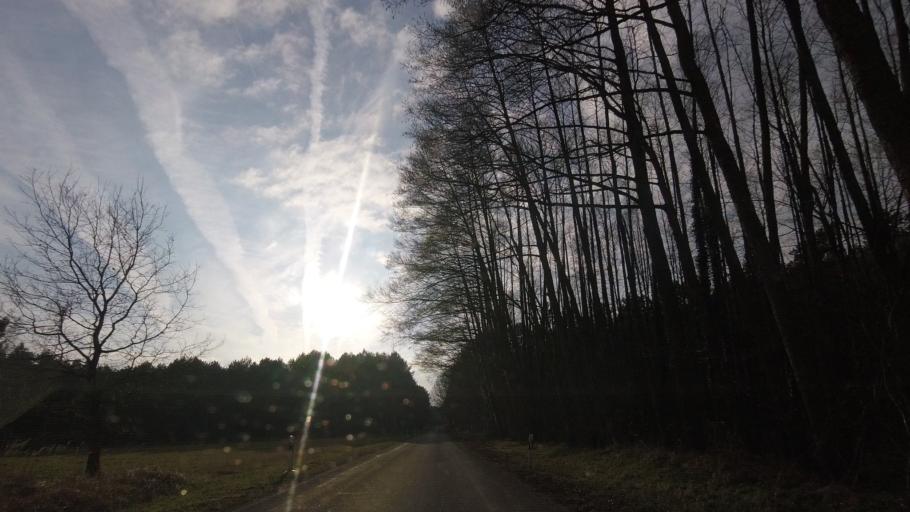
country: DE
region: Brandenburg
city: Belzig
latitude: 52.1319
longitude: 12.5727
